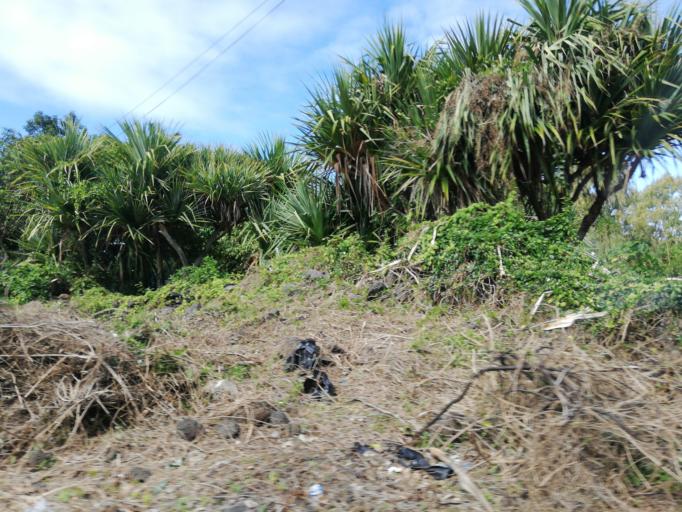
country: MU
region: Grand Port
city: Plaine Magnien
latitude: -20.4639
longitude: 57.6779
